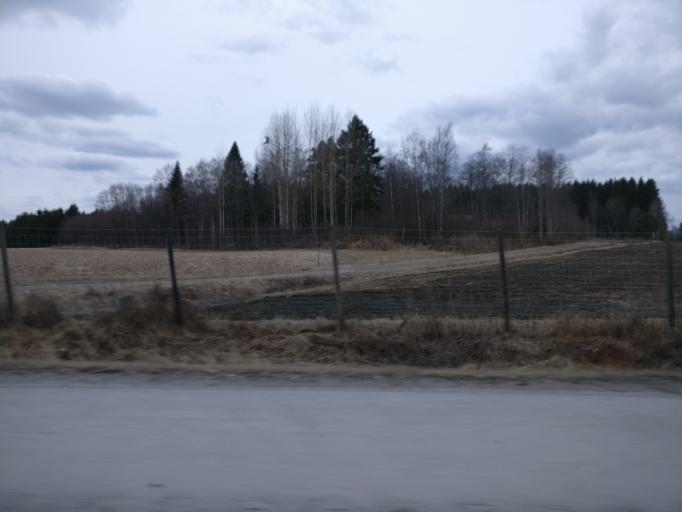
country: FI
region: Haeme
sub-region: Haemeenlinna
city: Janakkala
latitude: 60.9051
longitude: 24.5520
